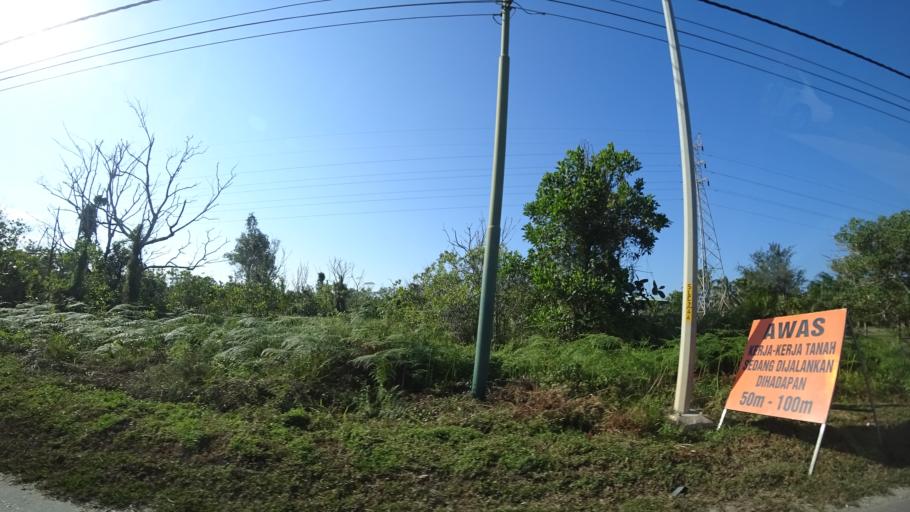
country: BN
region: Tutong
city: Tutong
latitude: 4.7209
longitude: 114.5450
